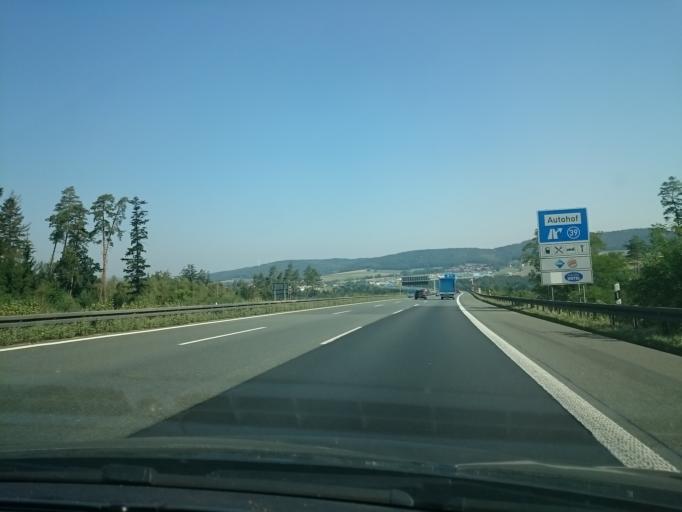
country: DE
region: Bavaria
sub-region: Upper Franconia
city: Himmelkron
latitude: 50.0359
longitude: 11.6090
